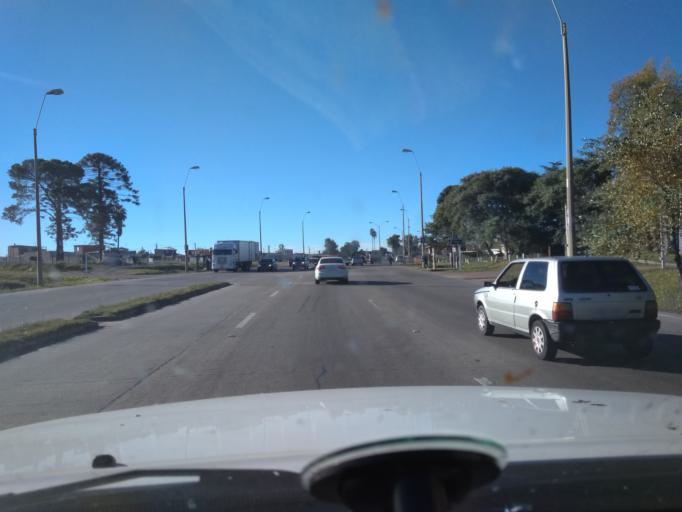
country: UY
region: Canelones
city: Colonia Nicolich
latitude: -34.7819
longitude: -56.0604
